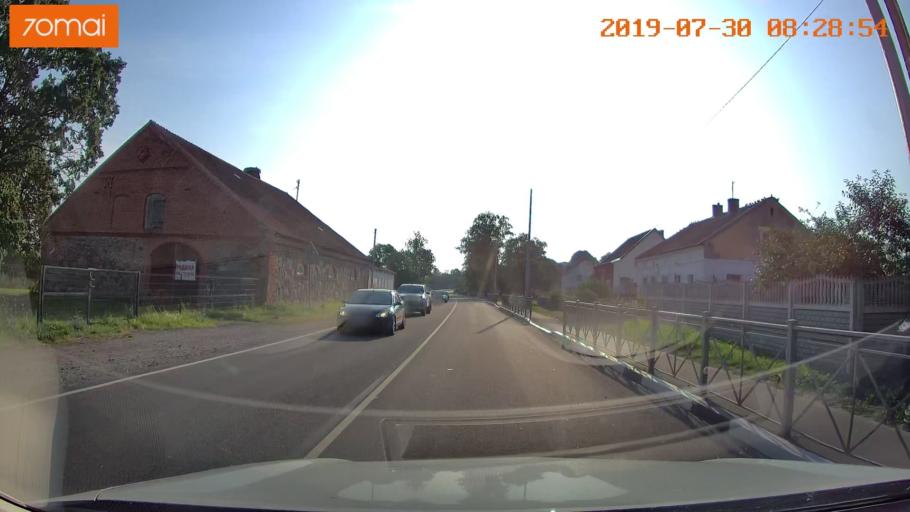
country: RU
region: Kaliningrad
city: Chernyakhovsk
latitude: 54.6306
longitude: 21.6534
